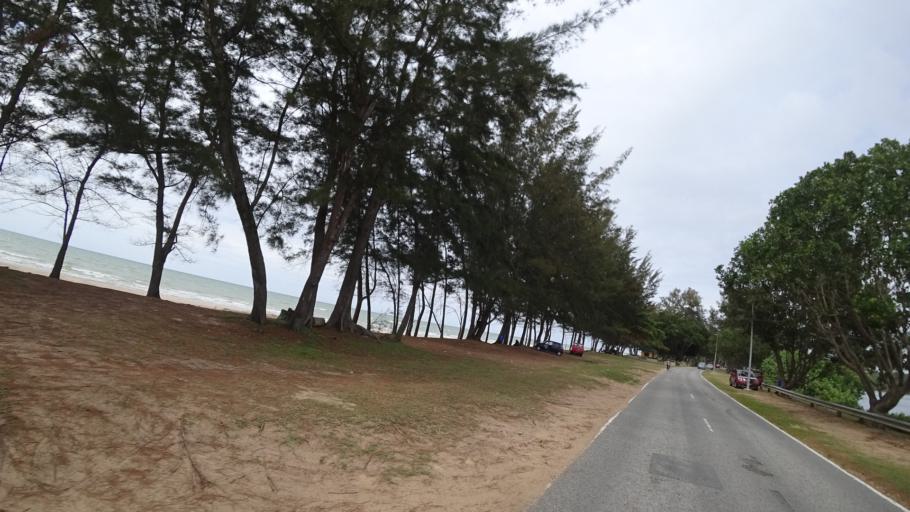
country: BN
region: Tutong
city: Tutong
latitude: 4.8049
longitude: 114.6349
